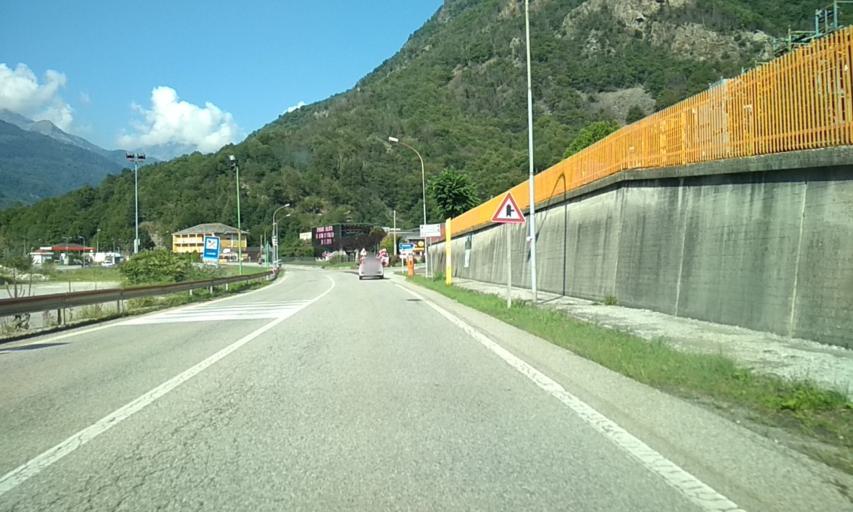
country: IT
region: Piedmont
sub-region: Provincia di Torino
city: Sparone
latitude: 45.4116
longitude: 7.5448
